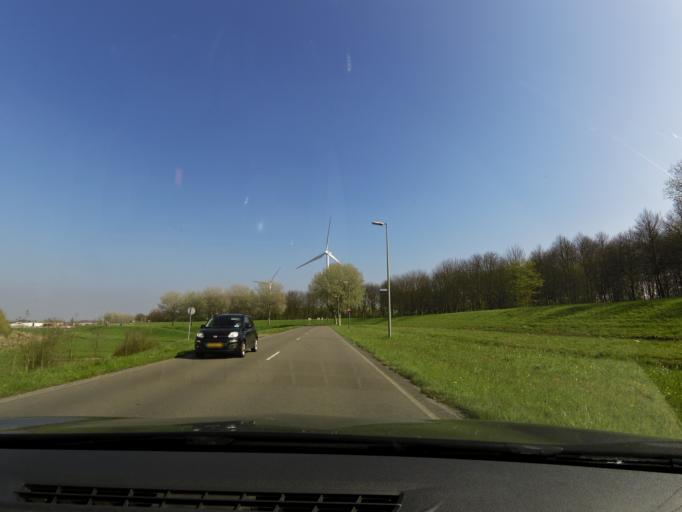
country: NL
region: South Holland
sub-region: Gemeente Maassluis
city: Maassluis
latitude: 51.9017
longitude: 4.2932
